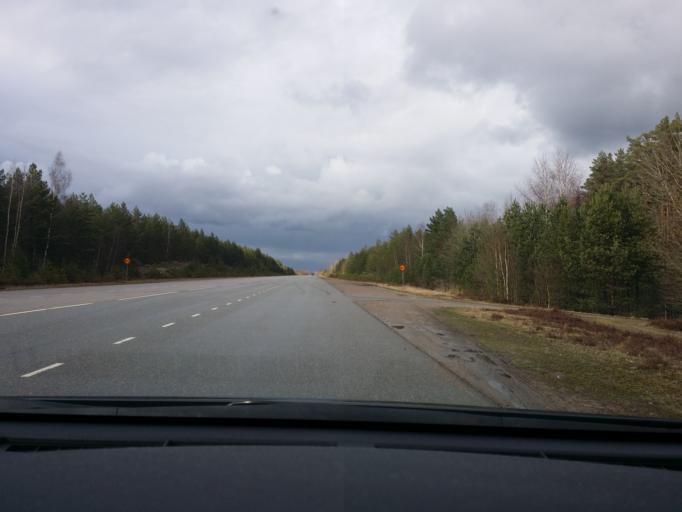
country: SE
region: Soedermanland
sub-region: Eskilstuna Kommun
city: Arla
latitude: 59.3247
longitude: 16.6816
